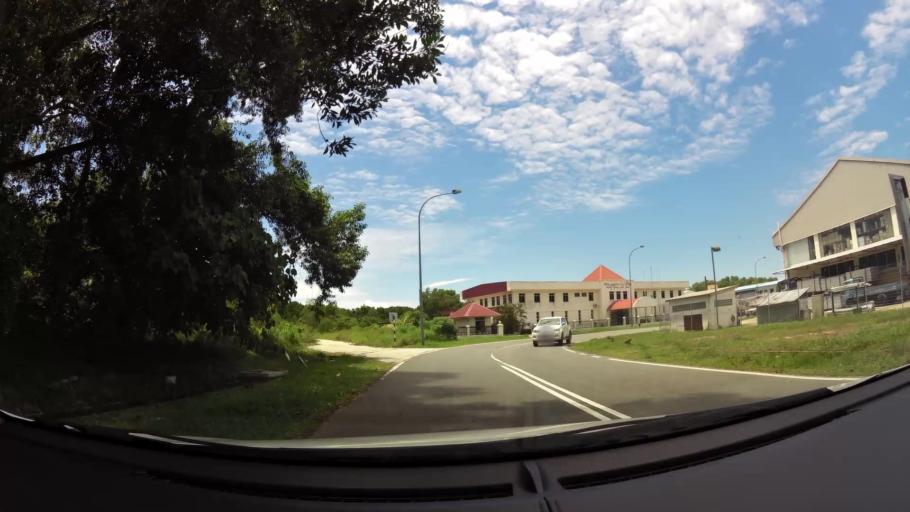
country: BN
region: Brunei and Muara
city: Bandar Seri Begawan
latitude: 5.0062
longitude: 115.0298
